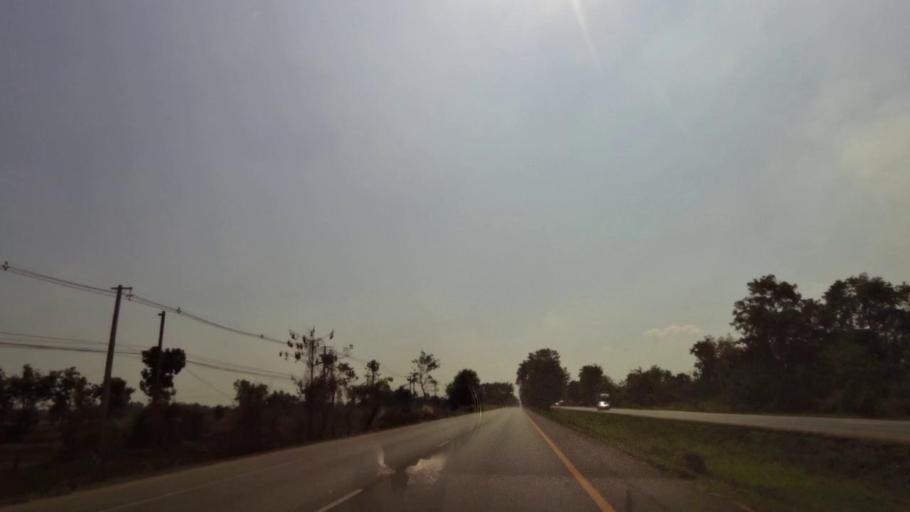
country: TH
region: Phichit
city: Bueng Na Rang
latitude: 16.2919
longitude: 100.1280
